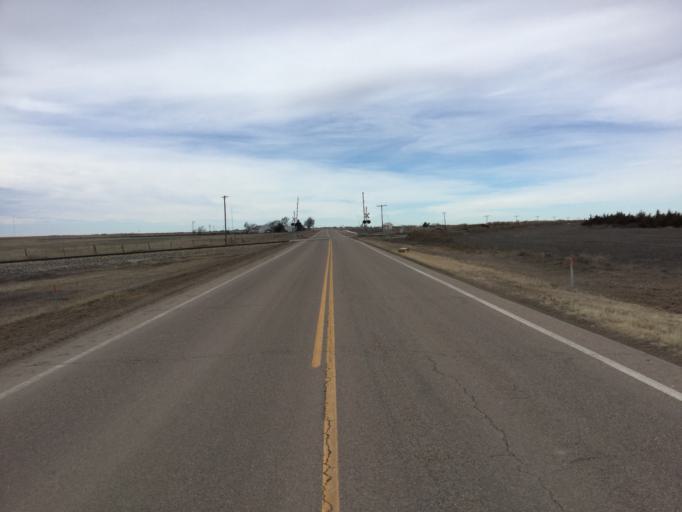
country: US
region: Kansas
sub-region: Lane County
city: Dighton
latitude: 38.4815
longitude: -100.4041
